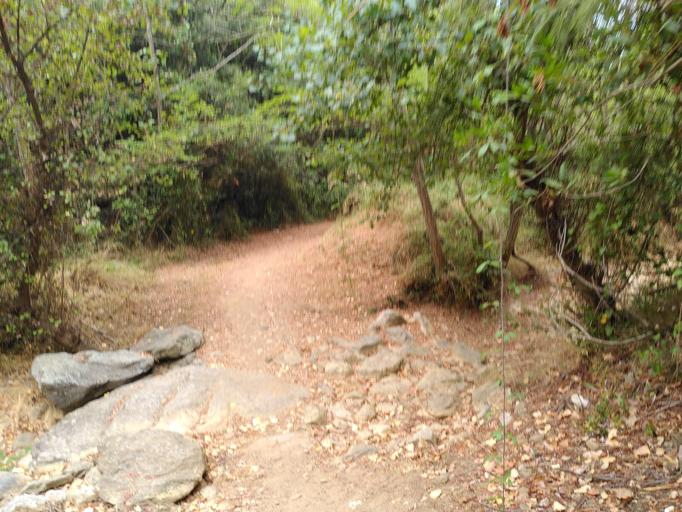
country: FR
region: Provence-Alpes-Cote d'Azur
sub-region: Departement du Var
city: Cavalaire-sur-Mer
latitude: 43.1656
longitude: 6.5157
